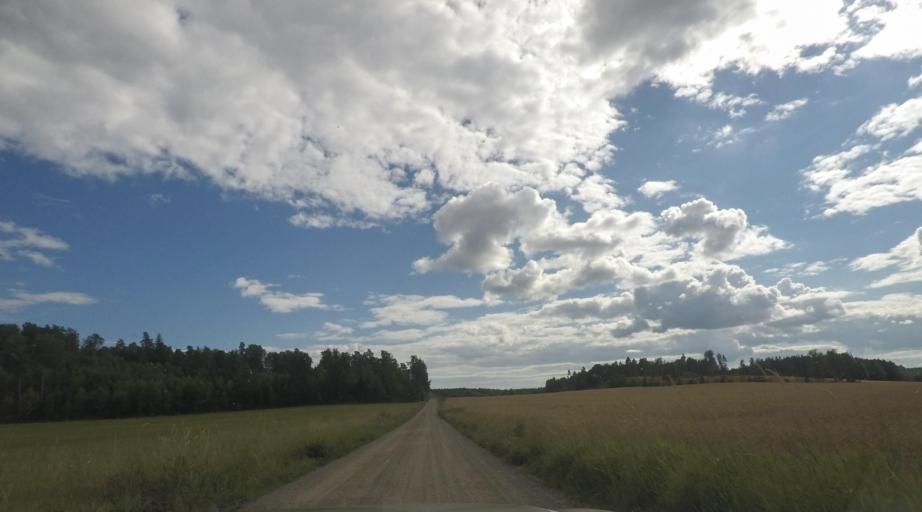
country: SE
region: Stockholm
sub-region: Sodertalje Kommun
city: Pershagen
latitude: 59.1192
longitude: 17.6568
